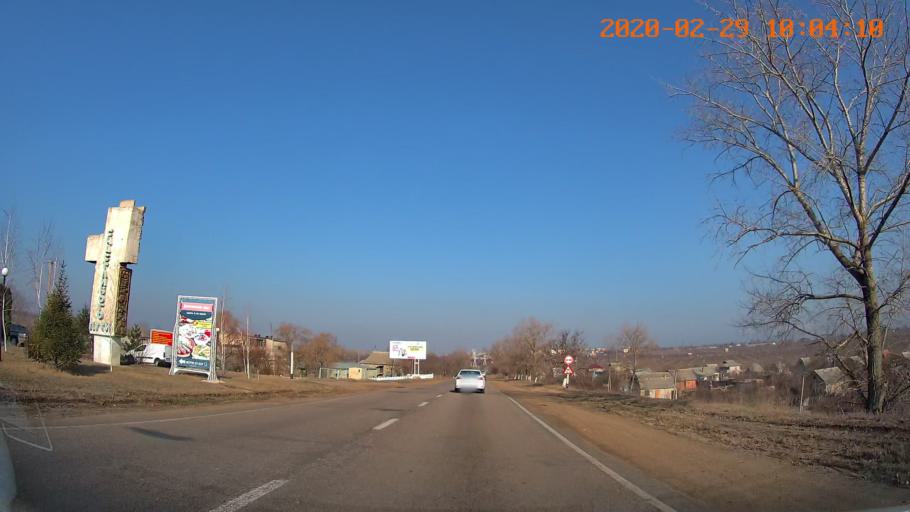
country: MD
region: Causeni
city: Chitcani
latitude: 46.7959
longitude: 29.6769
